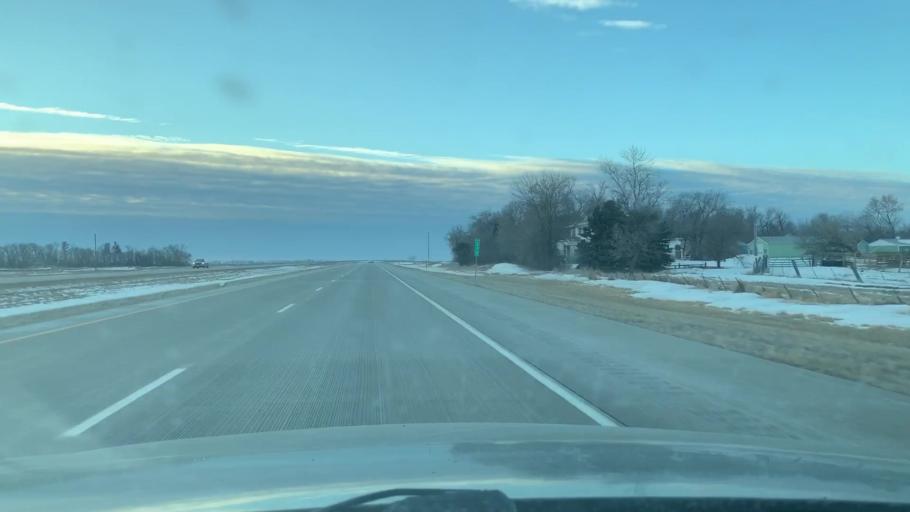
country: US
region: North Dakota
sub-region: Cass County
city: Casselton
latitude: 46.8758
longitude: -97.4680
